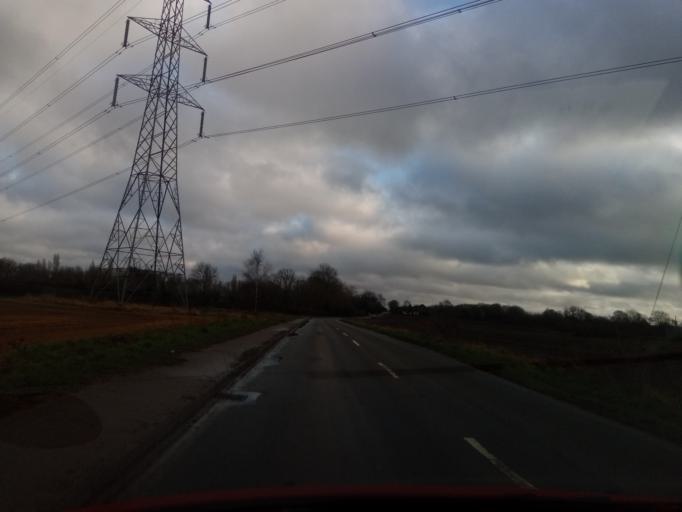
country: GB
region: England
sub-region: Derbyshire
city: Melbourne
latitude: 52.8498
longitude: -1.4180
